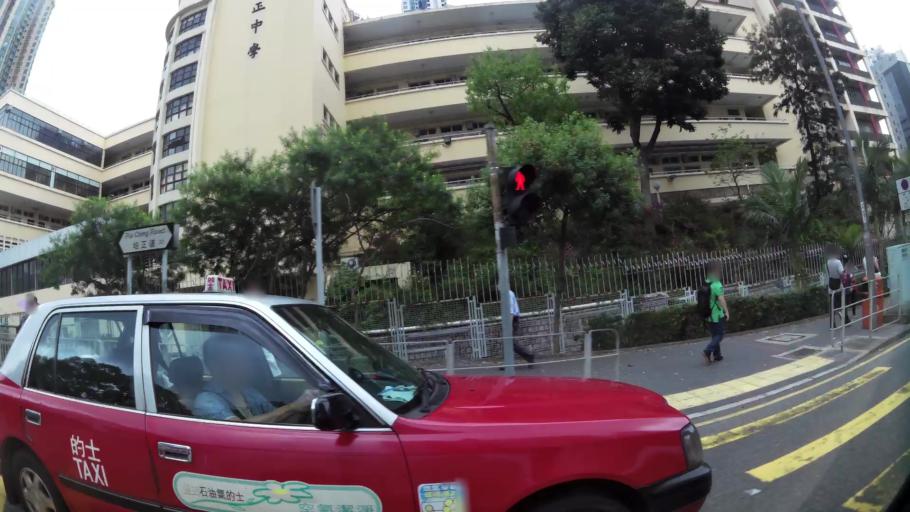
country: HK
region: Kowloon City
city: Kowloon
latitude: 22.3178
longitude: 114.1776
